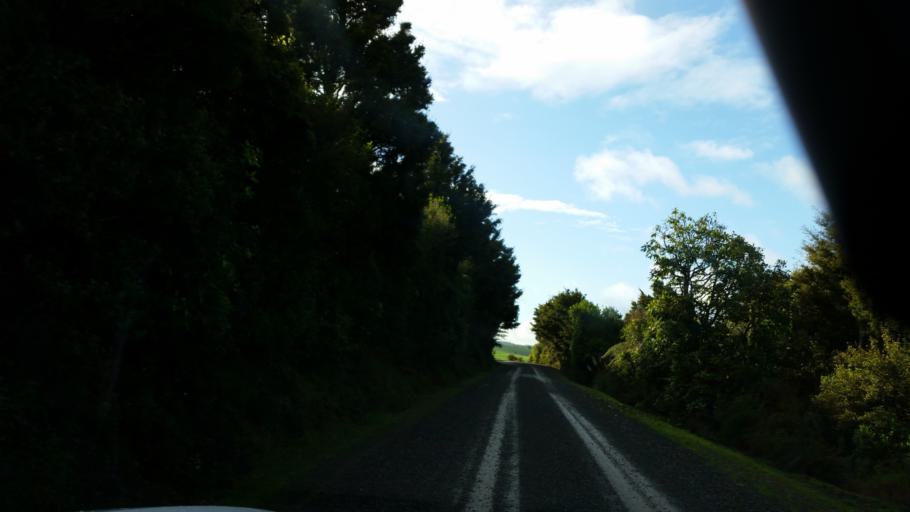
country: NZ
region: Northland
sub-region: Whangarei
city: Maungatapere
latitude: -35.6924
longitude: 174.1163
